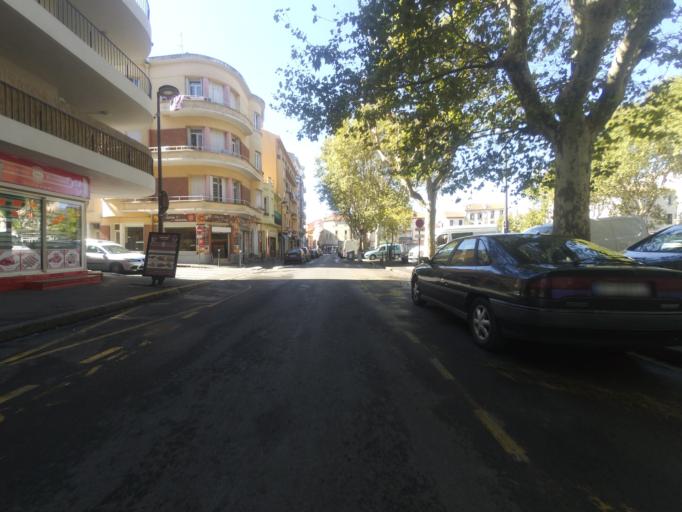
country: FR
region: Languedoc-Roussillon
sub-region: Departement des Pyrenees-Orientales
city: Perpignan
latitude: 42.6967
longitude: 2.9031
